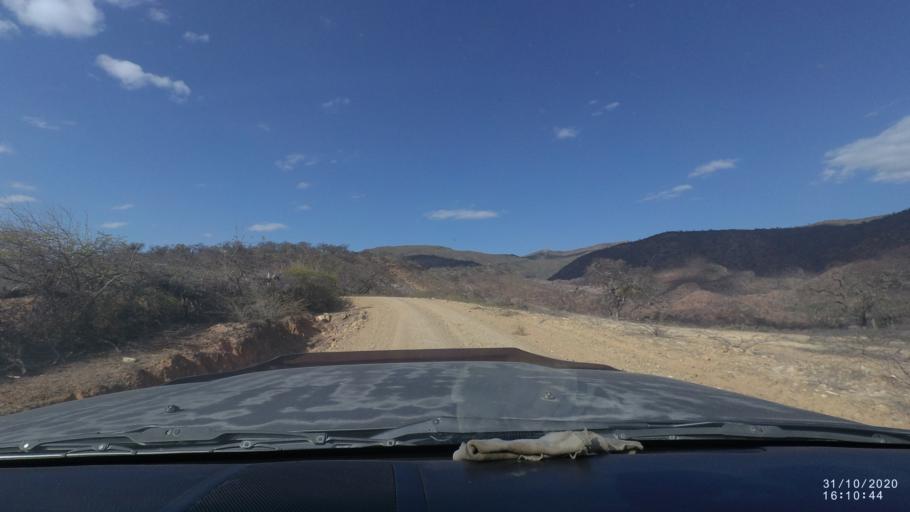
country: BO
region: Chuquisaca
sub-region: Provincia Zudanez
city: Mojocoya
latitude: -18.3827
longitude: -64.6274
